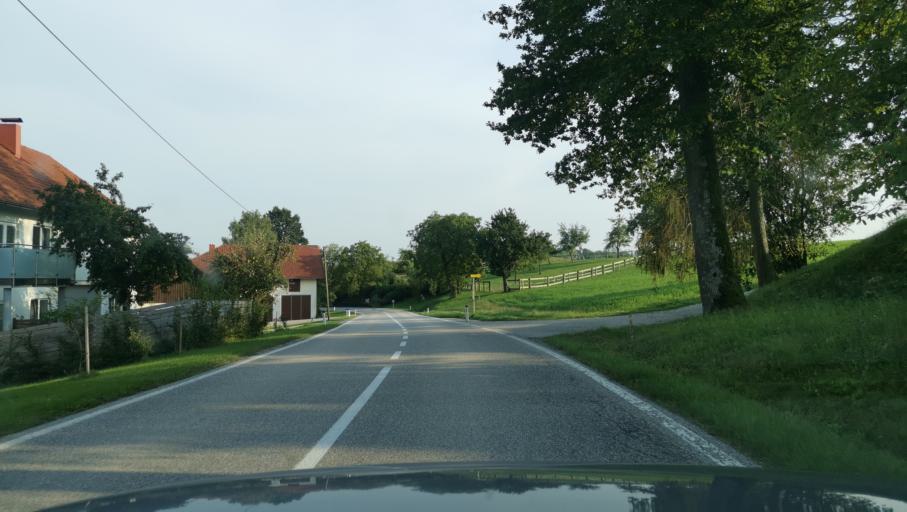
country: AT
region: Upper Austria
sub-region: Politischer Bezirk Grieskirchen
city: Grieskirchen
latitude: 48.3490
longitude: 13.7394
